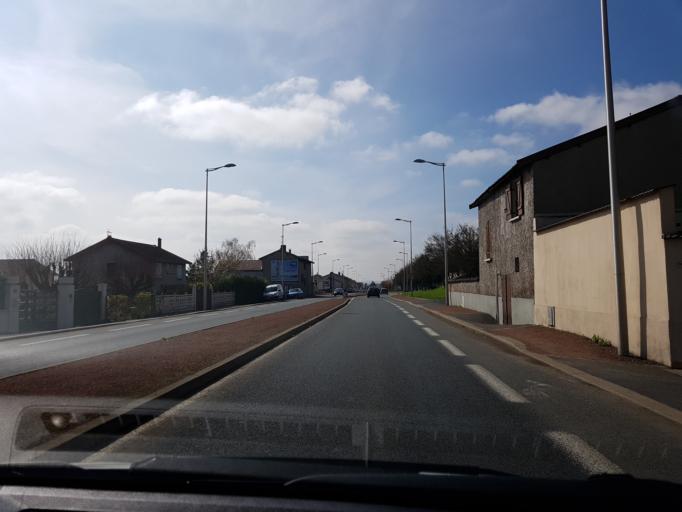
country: FR
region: Rhone-Alpes
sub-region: Departement du Rhone
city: Villefranche-sur-Saone
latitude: 45.9717
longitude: 4.7169
